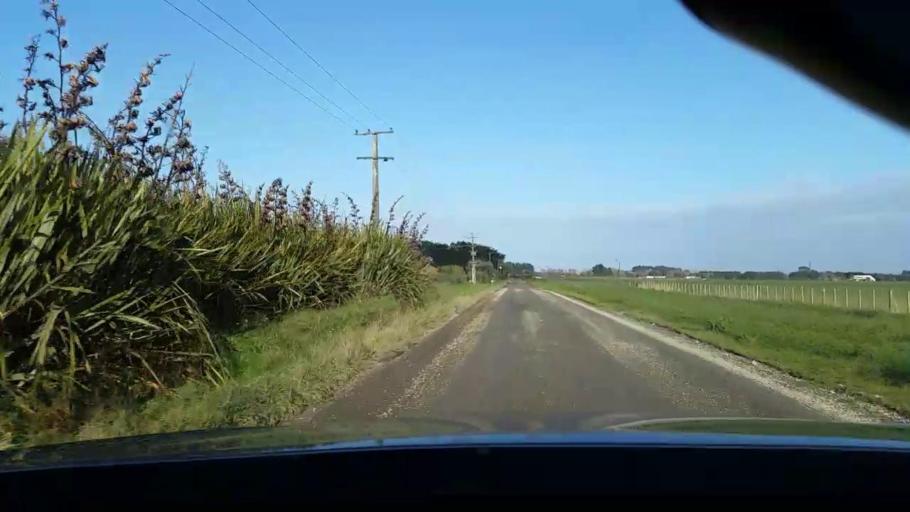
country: NZ
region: Southland
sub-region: Invercargill City
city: Invercargill
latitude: -46.3054
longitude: 168.3034
